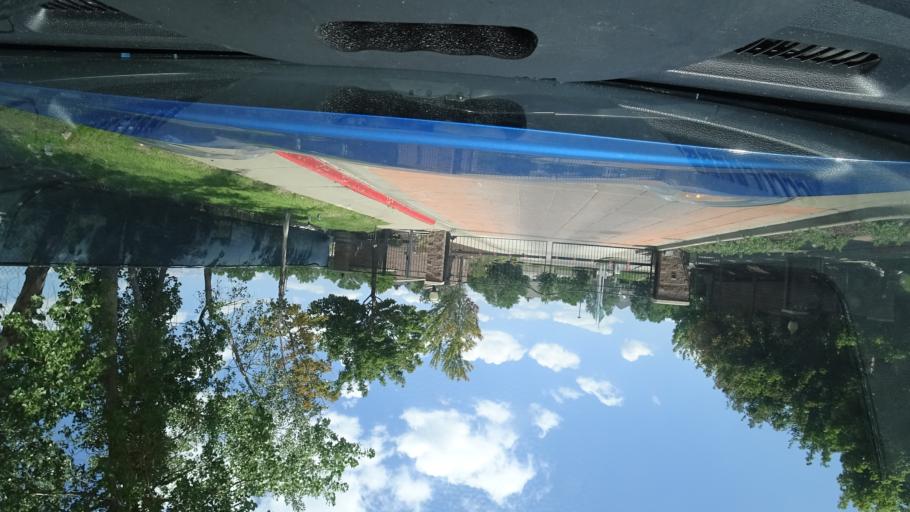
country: US
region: Colorado
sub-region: Arapahoe County
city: Glendale
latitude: 39.7009
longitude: -104.8915
